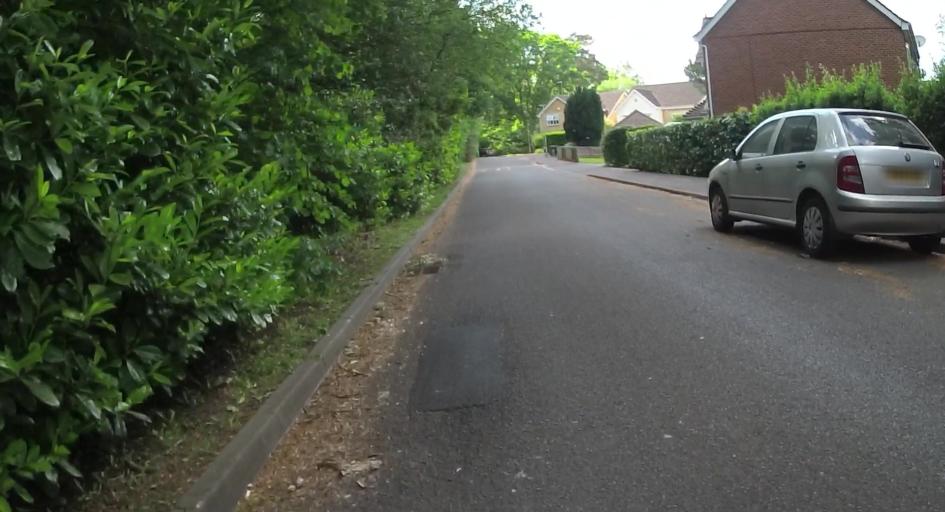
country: GB
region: England
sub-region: Bracknell Forest
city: Crowthorne
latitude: 51.3812
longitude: -0.7990
